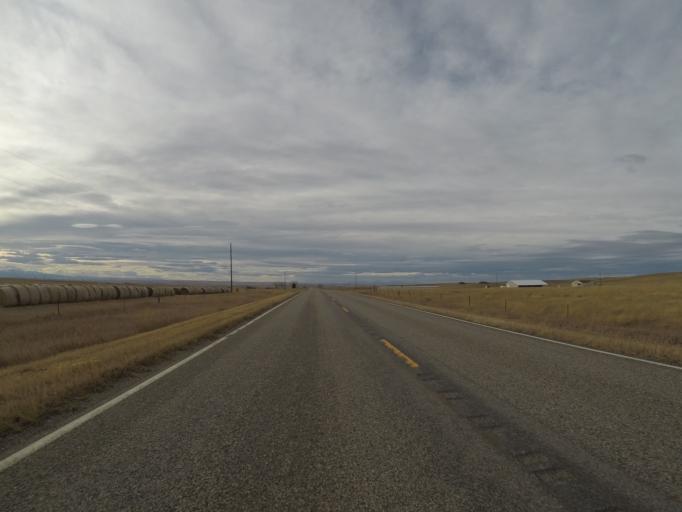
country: US
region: Montana
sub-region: Yellowstone County
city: Laurel
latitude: 45.8565
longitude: -108.8298
